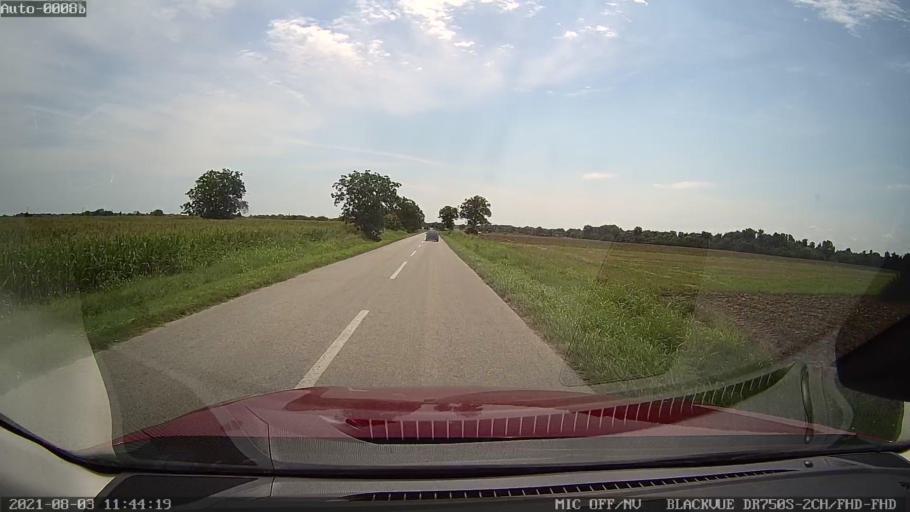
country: HR
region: Osjecko-Baranjska
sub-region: Grad Osijek
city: Bilje
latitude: 45.6038
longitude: 18.7706
